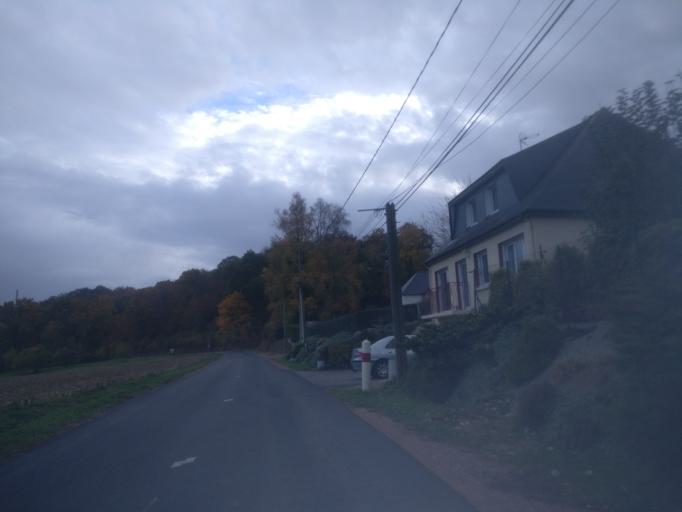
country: FR
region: Brittany
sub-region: Departement d'Ille-et-Vilaine
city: Guichen
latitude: 48.0051
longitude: -1.7921
